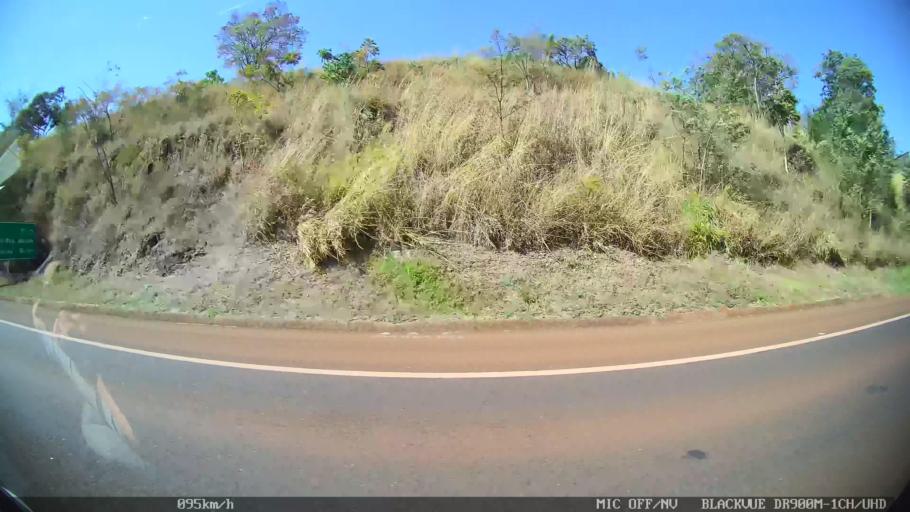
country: BR
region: Sao Paulo
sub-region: Franca
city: Franca
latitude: -20.6241
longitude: -47.4617
